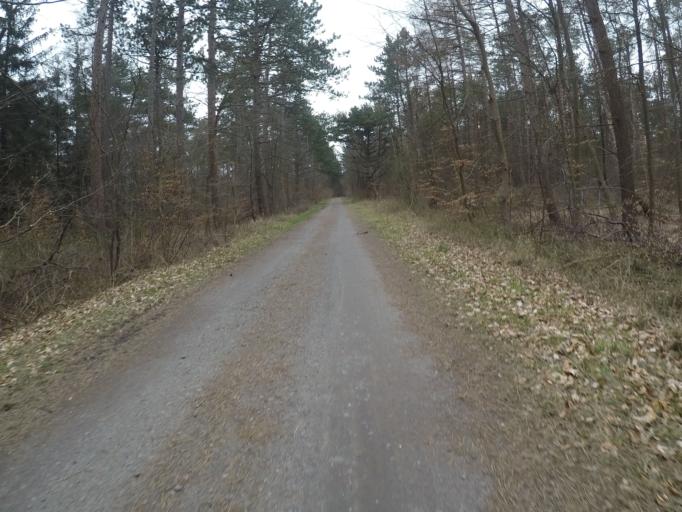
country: DE
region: Lower Saxony
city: Nordholz
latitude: 53.8180
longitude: 8.6380
